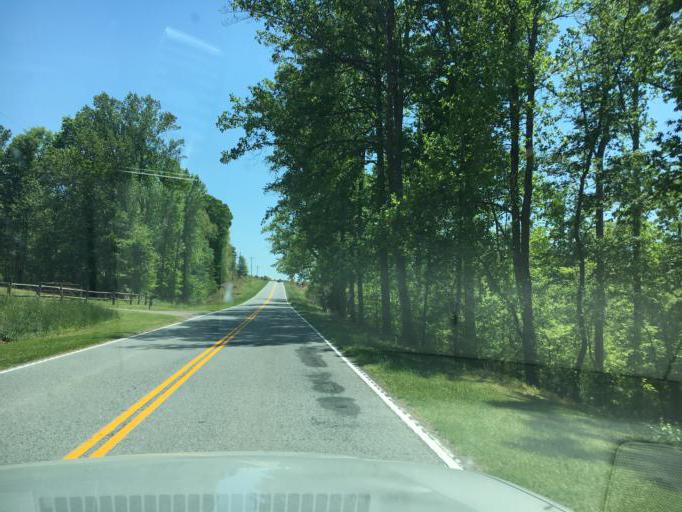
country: US
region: South Carolina
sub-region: Cherokee County
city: Blacksburg
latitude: 35.1545
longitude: -81.5751
